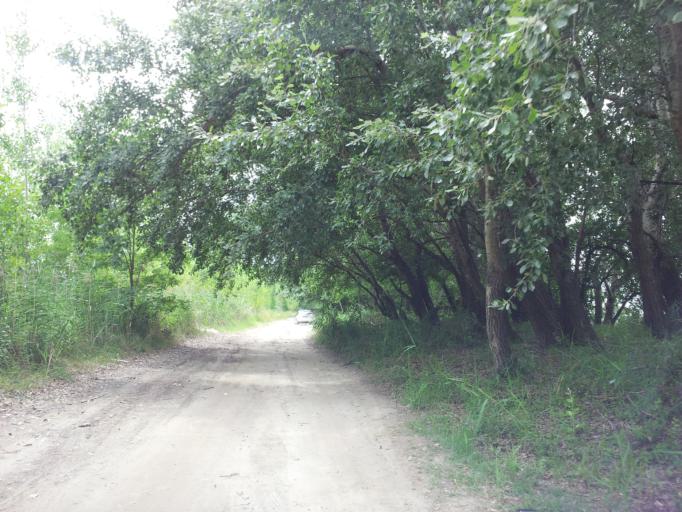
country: HU
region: Pest
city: Szigetcsep
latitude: 47.2265
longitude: 18.9706
